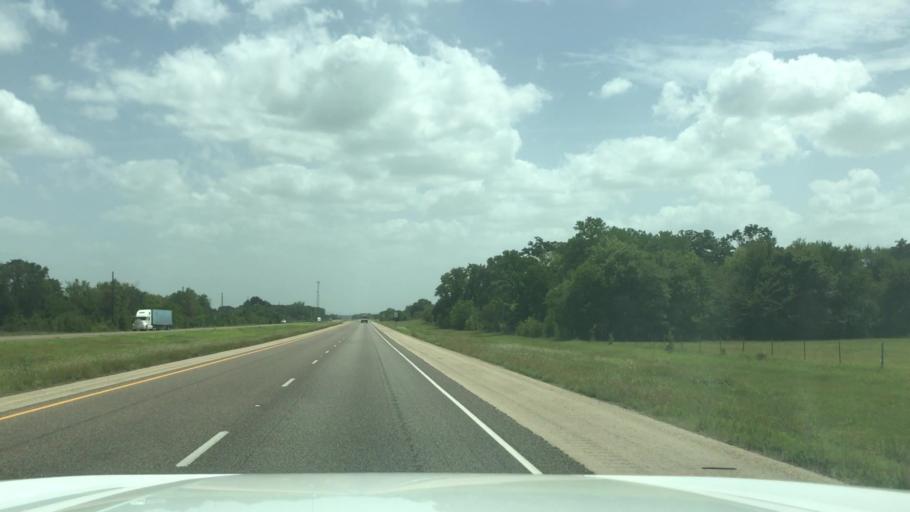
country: US
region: Texas
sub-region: Robertson County
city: Calvert
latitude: 31.0449
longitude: -96.7107
